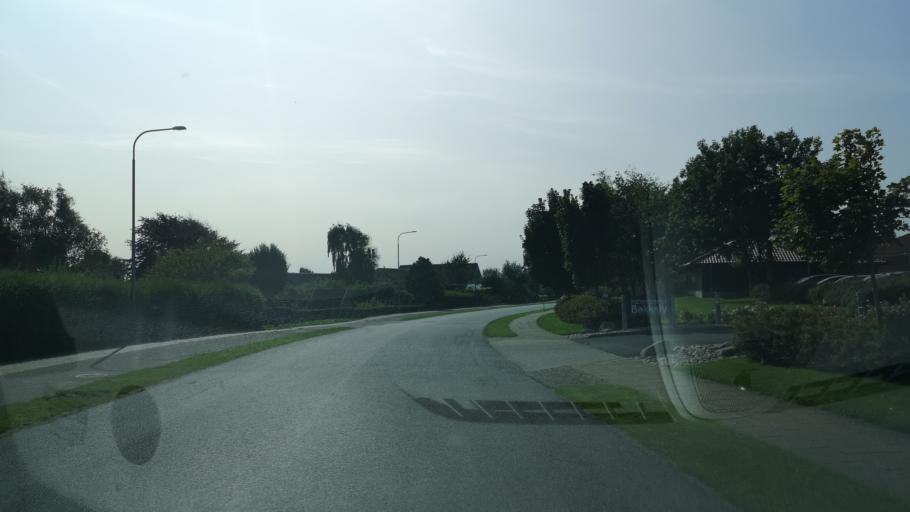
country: DK
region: Central Jutland
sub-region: Ringkobing-Skjern Kommune
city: Videbaek
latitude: 56.0852
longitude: 8.6229
